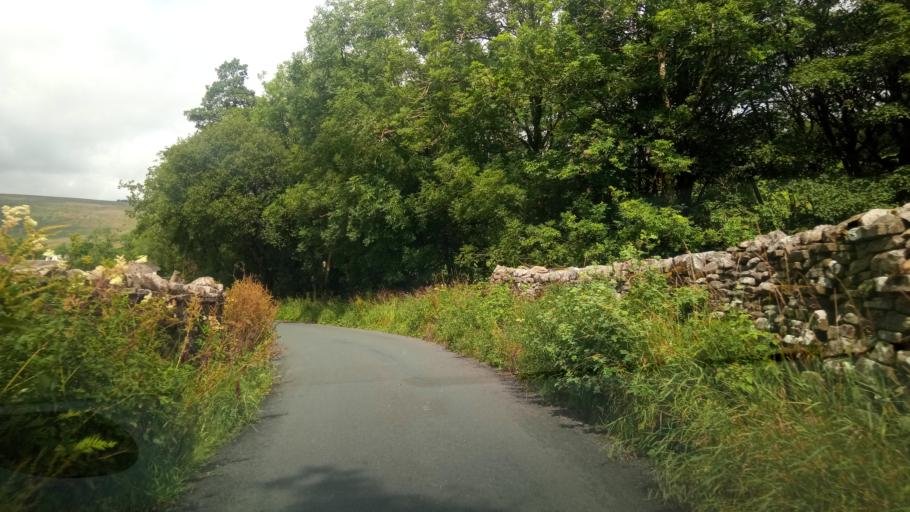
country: GB
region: England
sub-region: North Yorkshire
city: Ingleton
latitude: 54.2703
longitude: -2.3550
